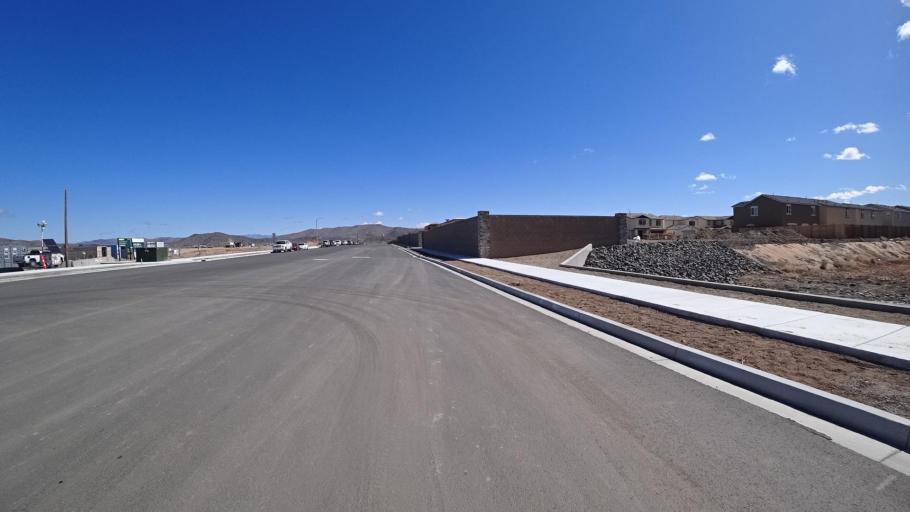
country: US
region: Nevada
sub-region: Washoe County
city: Lemmon Valley
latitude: 39.6467
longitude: -119.8572
